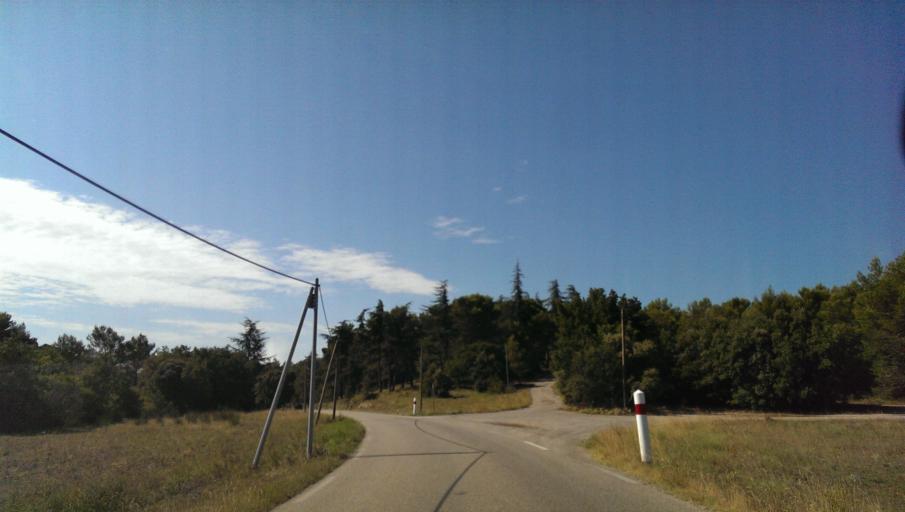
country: FR
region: Provence-Alpes-Cote d'Azur
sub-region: Departement du Vaucluse
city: Gordes
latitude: 43.9406
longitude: 5.2095
